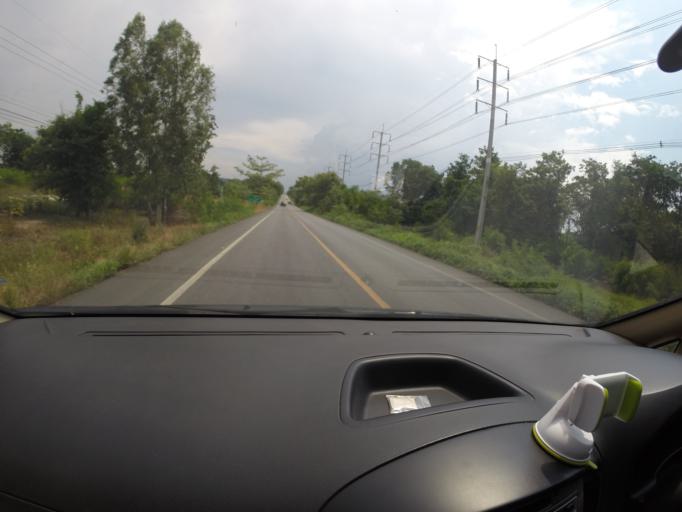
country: TH
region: Lop Buri
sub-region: Amphoe Lam Sonthi
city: Lam Sonthi
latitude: 15.1126
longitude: 101.4630
